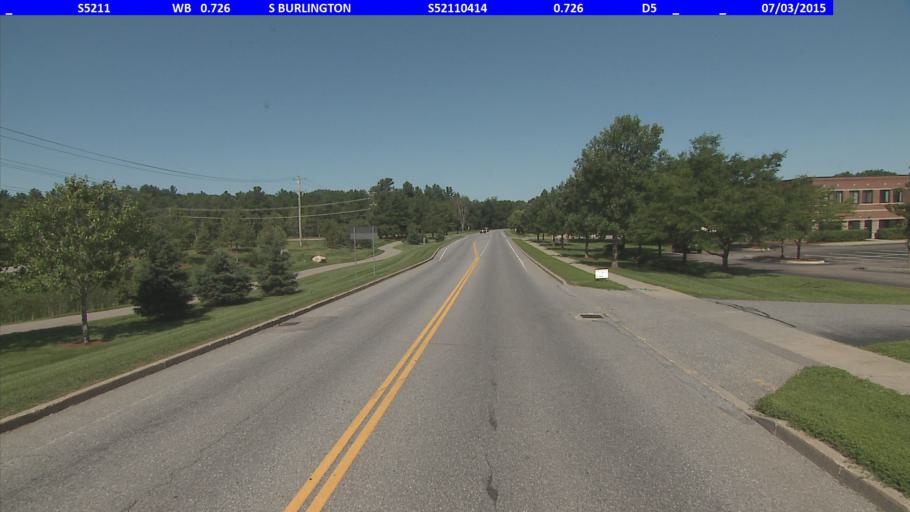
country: US
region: Vermont
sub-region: Chittenden County
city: South Burlington
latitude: 44.4540
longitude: -73.1438
